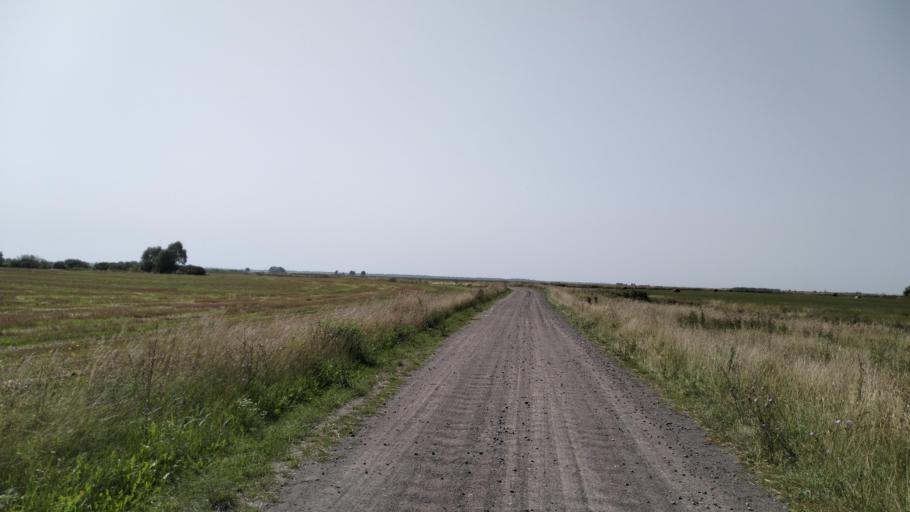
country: BY
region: Brest
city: Davyd-Haradok
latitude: 52.0117
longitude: 27.1663
